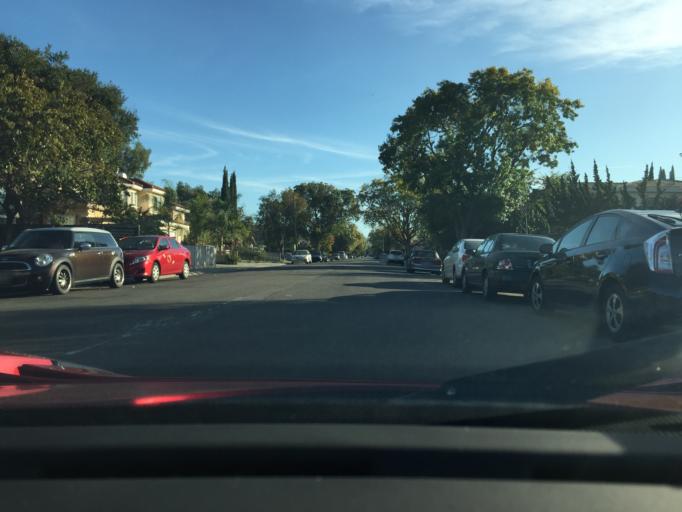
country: US
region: California
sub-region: Santa Clara County
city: Cupertino
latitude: 37.3222
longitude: -122.0034
